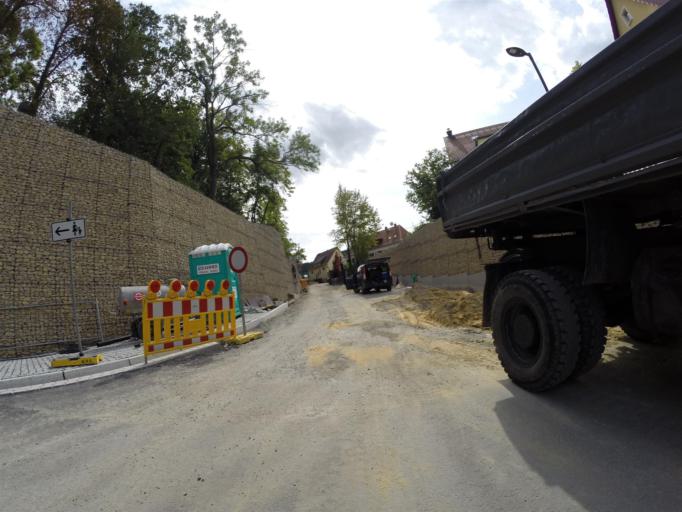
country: DE
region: Thuringia
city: Jena
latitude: 50.9247
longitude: 11.5965
